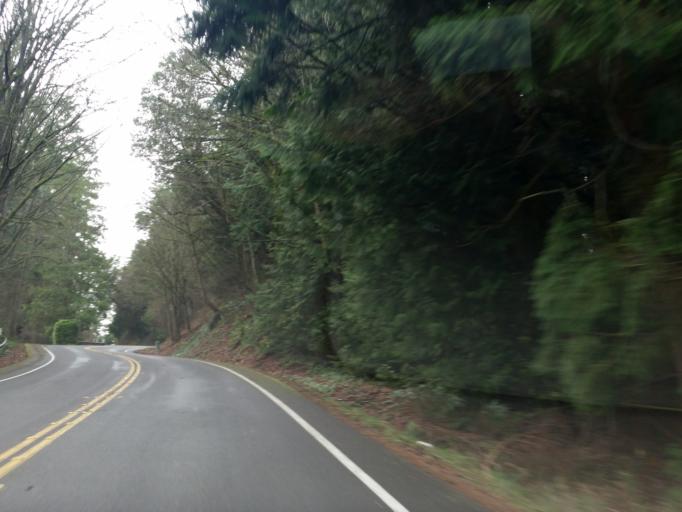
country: US
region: Washington
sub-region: King County
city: Shoreline
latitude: 47.7560
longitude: -122.3664
